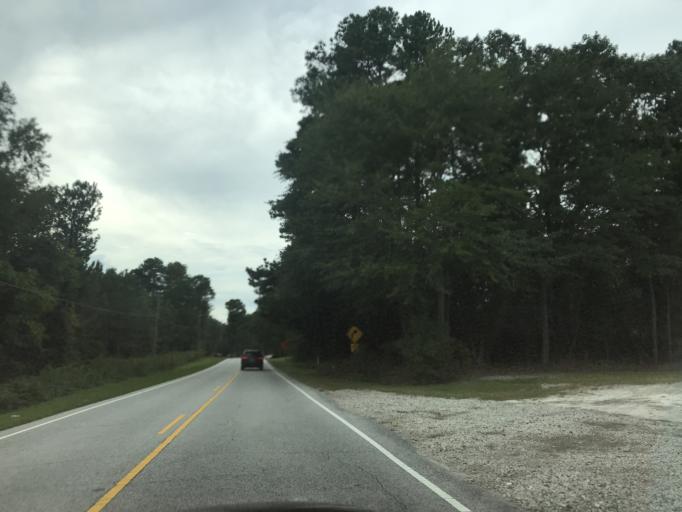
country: US
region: North Carolina
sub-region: Franklin County
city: Youngsville
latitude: 35.9985
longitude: -78.4223
